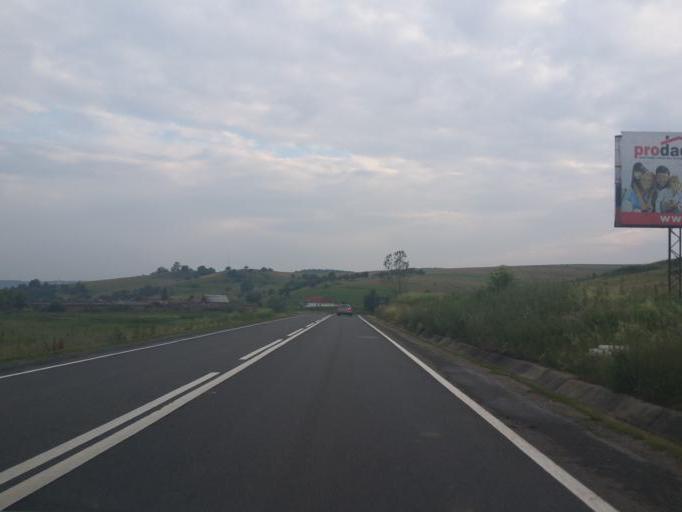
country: RO
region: Cluj
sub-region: Comuna Sanpaul
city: Sanpaul
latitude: 46.9145
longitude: 23.4199
